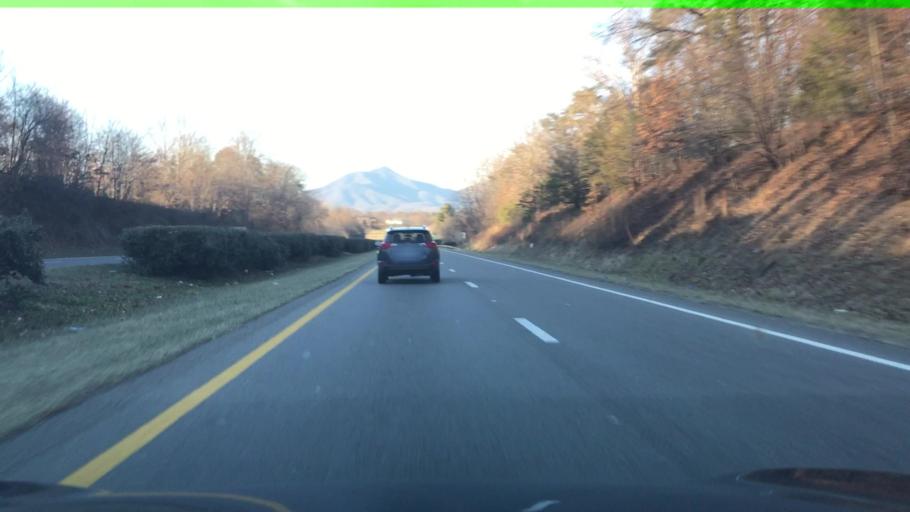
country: US
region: Virginia
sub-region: City of Bedford
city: Bedford
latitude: 37.3292
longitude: -79.5409
